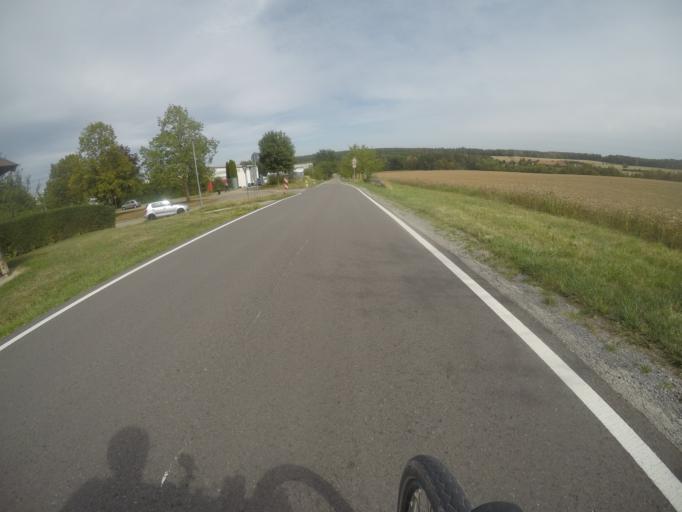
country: DE
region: Baden-Wuerttemberg
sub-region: Karlsruhe Region
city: Eutingen
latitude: 48.8849
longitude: 8.7578
